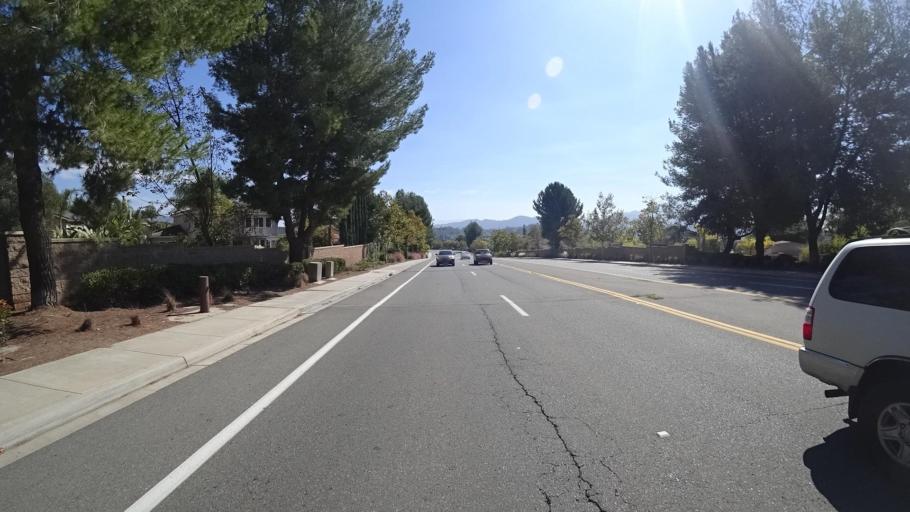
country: US
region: California
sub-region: San Diego County
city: Rancho San Diego
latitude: 32.7656
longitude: -116.9232
